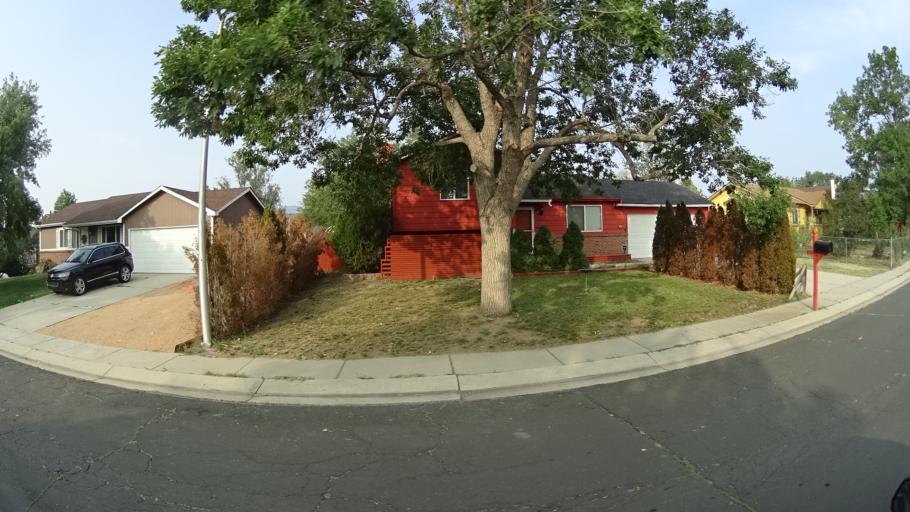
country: US
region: Colorado
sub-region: El Paso County
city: Stratmoor
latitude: 38.8013
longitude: -104.7468
